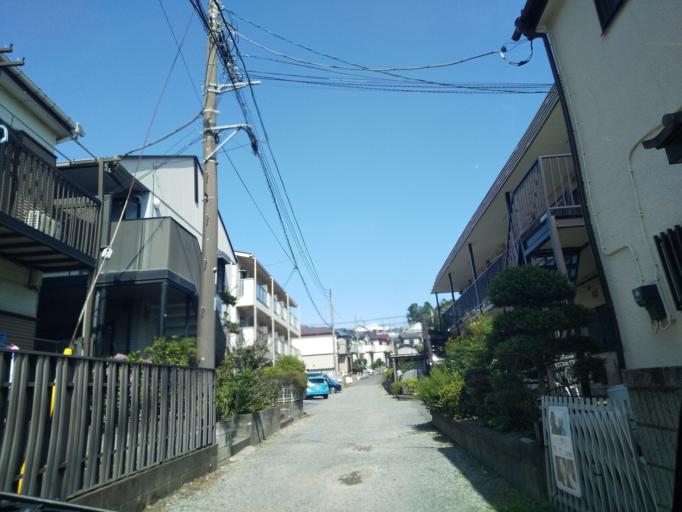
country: JP
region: Kanagawa
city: Zama
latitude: 35.4636
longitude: 139.4148
